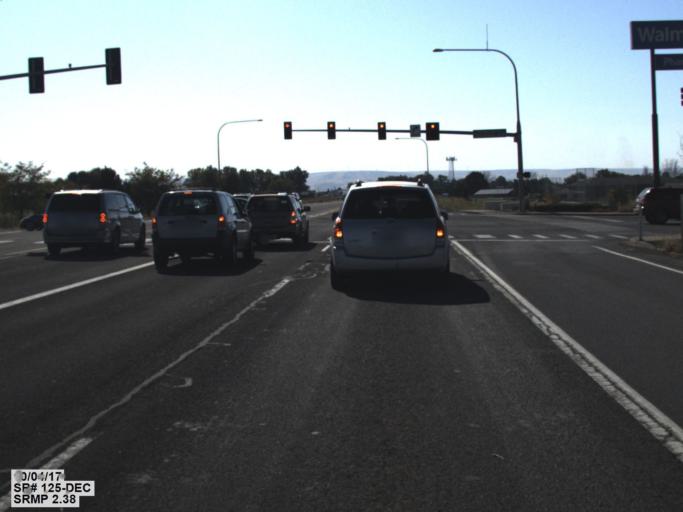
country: US
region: Washington
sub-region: Walla Walla County
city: College Place
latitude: 46.0322
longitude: -118.3800
